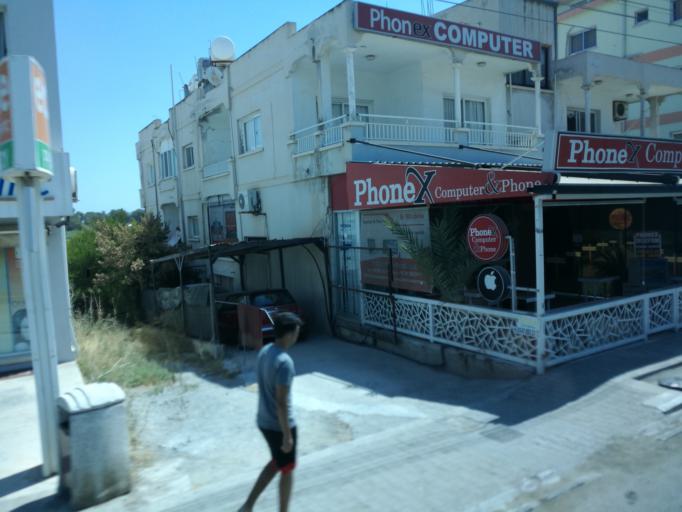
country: CY
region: Ammochostos
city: Famagusta
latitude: 35.1369
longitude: 33.9206
